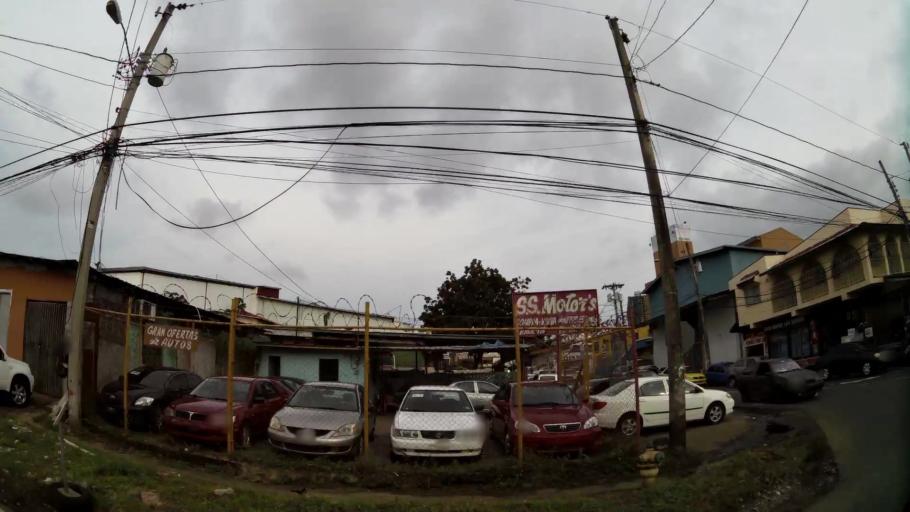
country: PA
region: Panama
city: Panama
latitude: 9.0023
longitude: -79.5217
